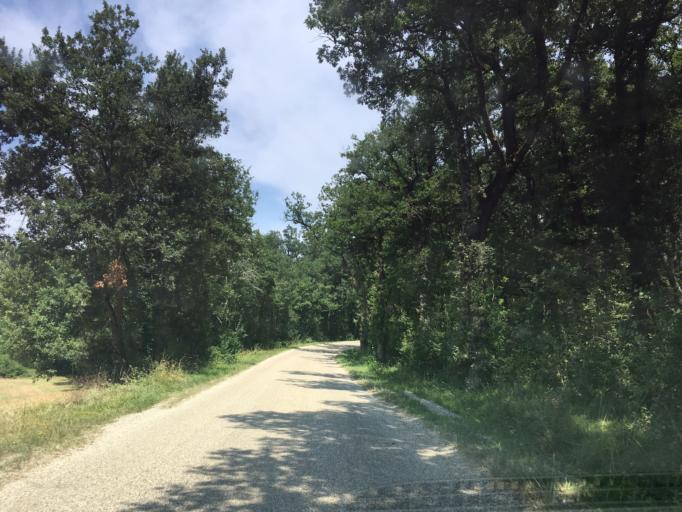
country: FR
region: Midi-Pyrenees
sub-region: Departement du Gers
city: Jegun
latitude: 43.7919
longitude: 0.4874
